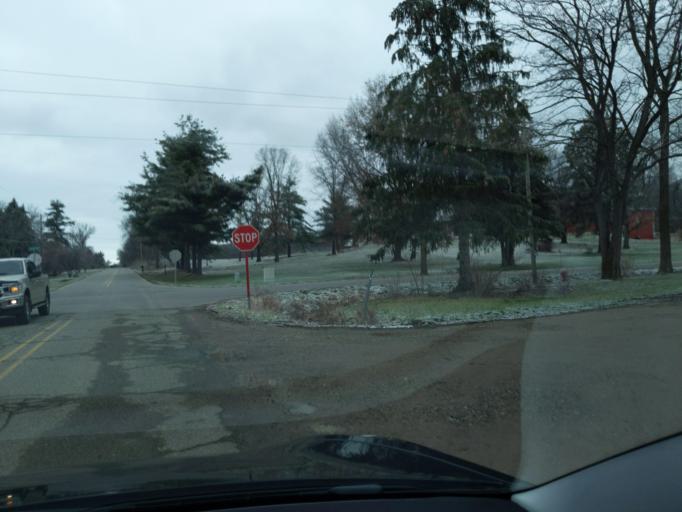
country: US
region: Michigan
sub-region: Jackson County
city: Spring Arbor
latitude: 42.2181
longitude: -84.5165
